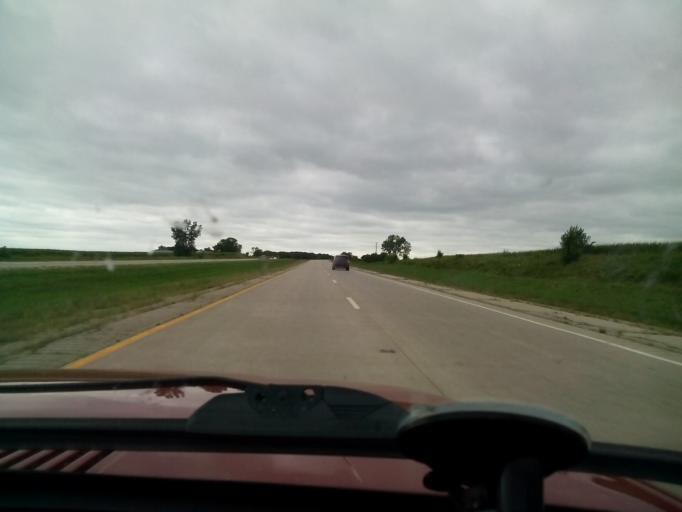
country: US
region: Wisconsin
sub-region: Columbia County
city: Columbus
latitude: 43.2786
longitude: -89.0893
